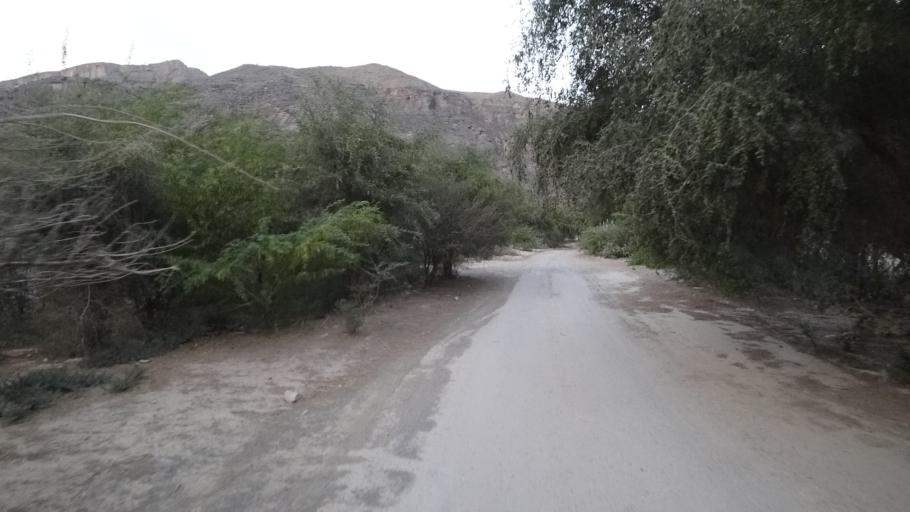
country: OM
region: Muhafazat ad Dakhiliyah
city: Nizwa
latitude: 23.0650
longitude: 57.4698
